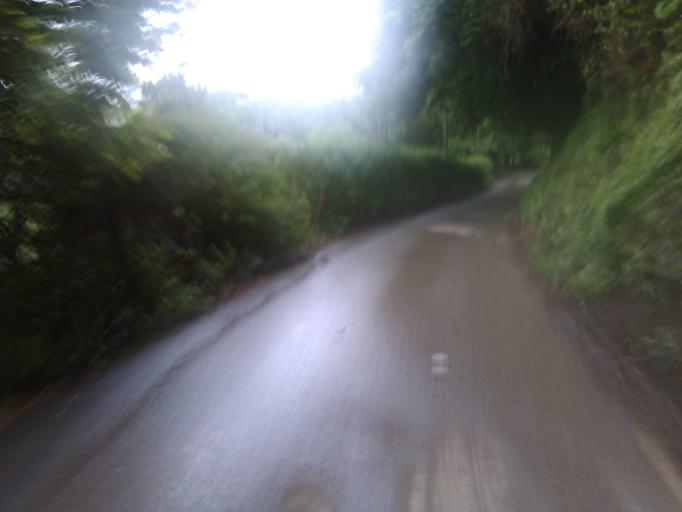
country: ES
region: Basque Country
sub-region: Provincia de Guipuzcoa
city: Astigarraga
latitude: 43.2782
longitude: -1.9576
